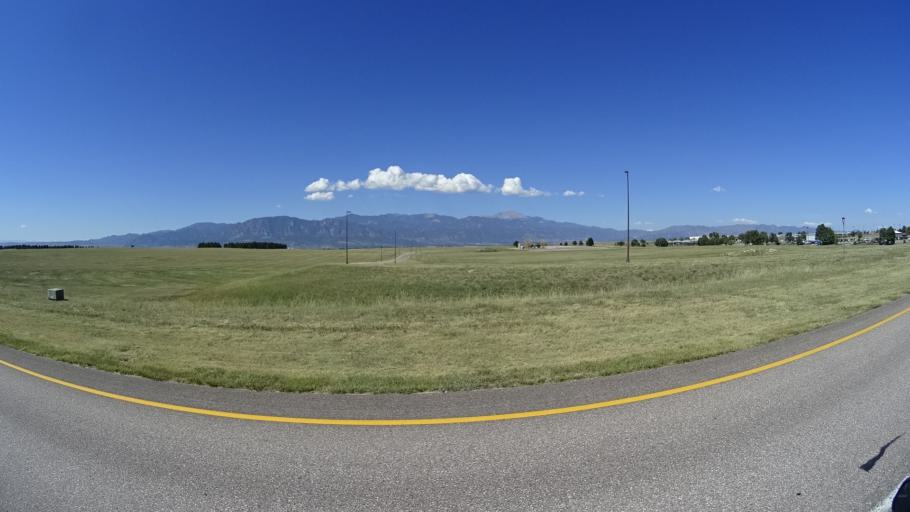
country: US
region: Colorado
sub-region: El Paso County
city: Security-Widefield
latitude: 38.7883
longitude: -104.6972
